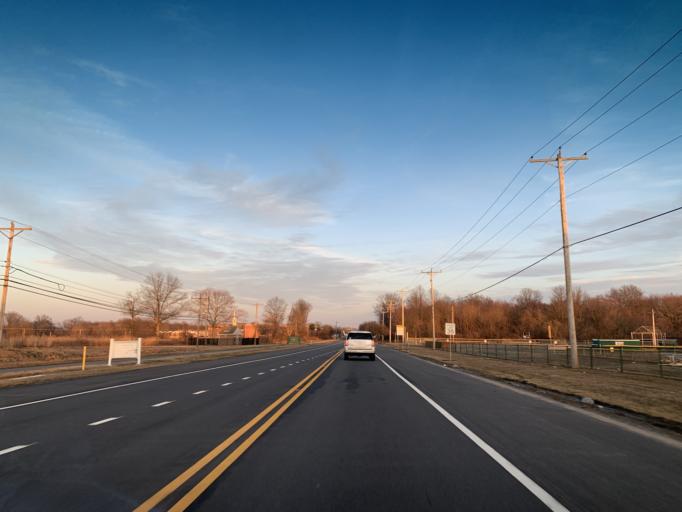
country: US
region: Delaware
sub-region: New Castle County
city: New Castle
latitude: 39.6645
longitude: -75.5860
